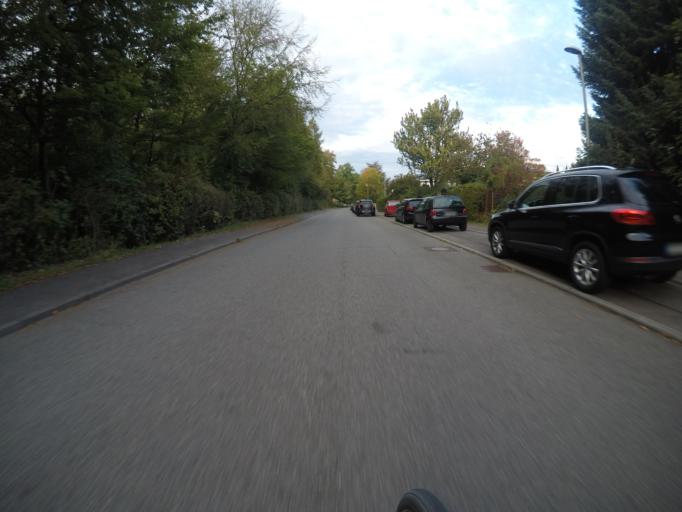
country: DE
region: Baden-Wuerttemberg
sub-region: Regierungsbezirk Stuttgart
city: Steinenbronn
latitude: 48.7191
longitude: 9.0891
